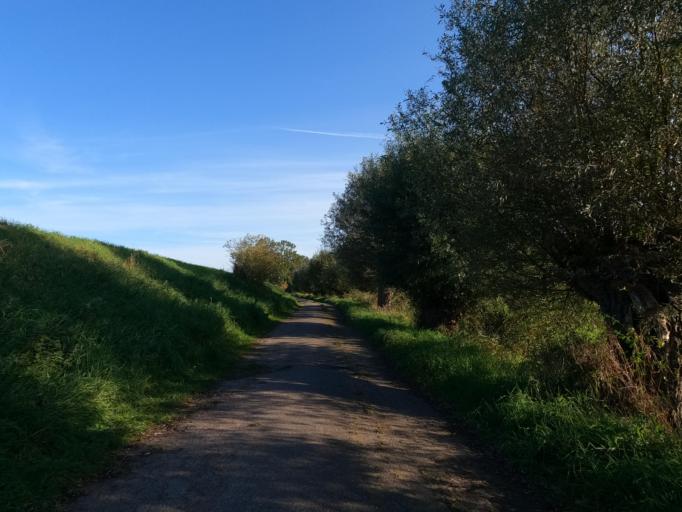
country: DE
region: Schleswig-Holstein
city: Neukirchen
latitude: 54.3126
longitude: 11.0273
